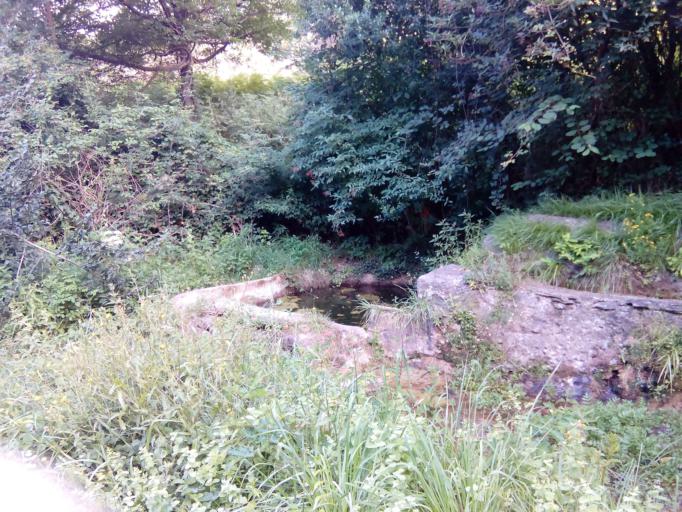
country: ES
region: Basque Country
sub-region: Provincia de Guipuzcoa
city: Andoain
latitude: 43.2273
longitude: -2.0233
